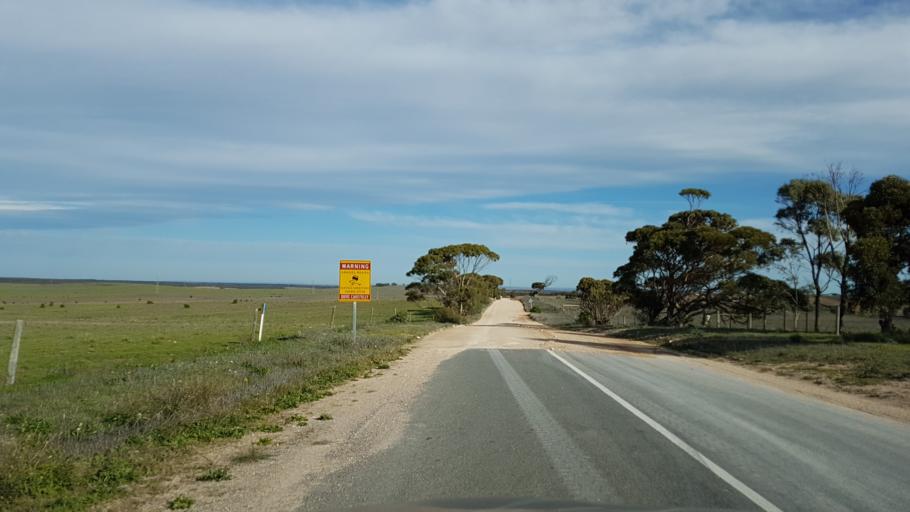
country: AU
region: South Australia
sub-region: Murray Bridge
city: Tailem Bend
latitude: -35.1832
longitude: 139.4550
